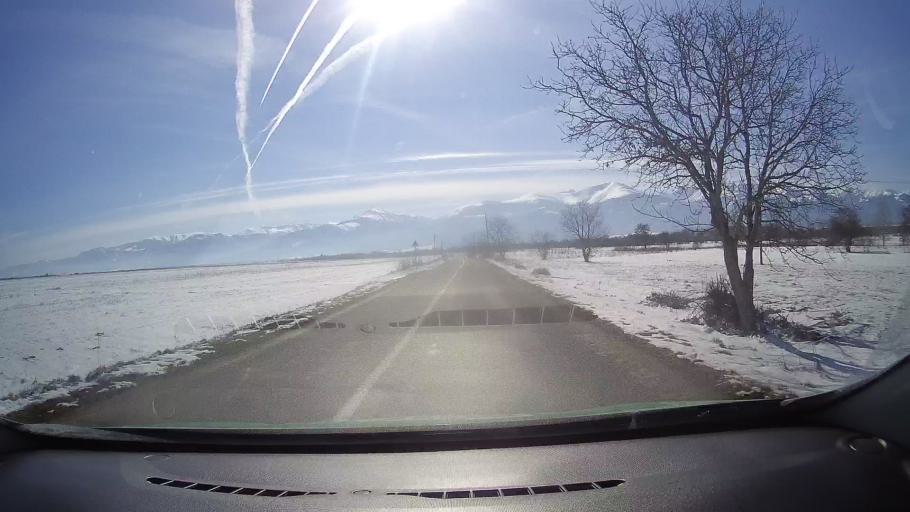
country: RO
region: Brasov
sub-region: Comuna Sambata de Sus
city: Sambata de Sus
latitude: 45.7454
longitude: 24.8430
